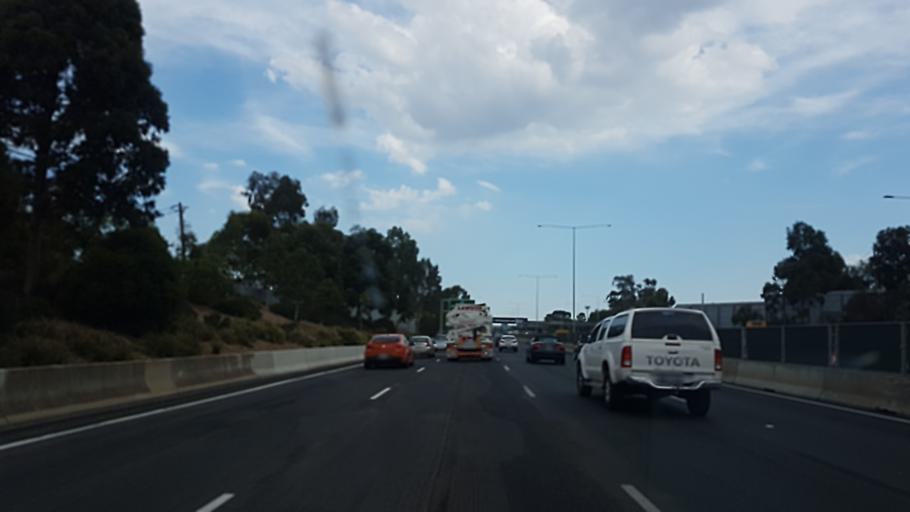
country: AU
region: Victoria
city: Brunswick West
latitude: -37.7590
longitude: 144.9381
